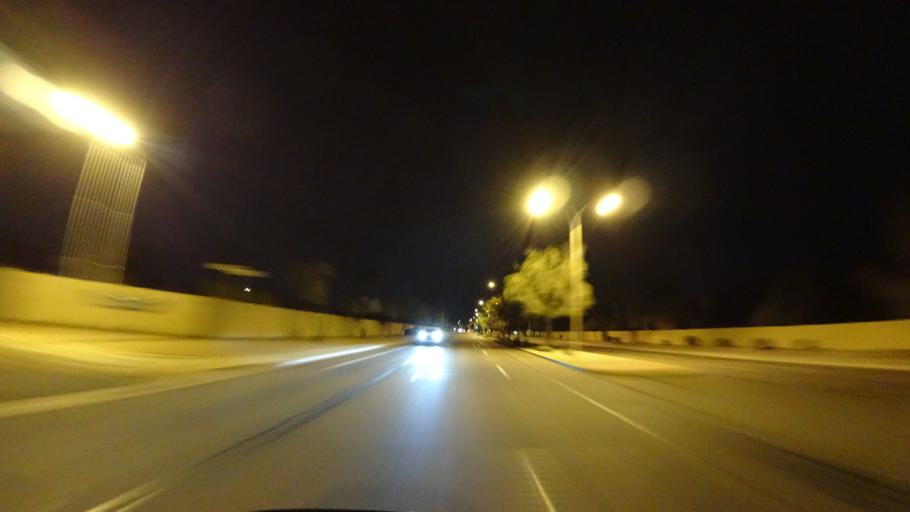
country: US
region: Arizona
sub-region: Maricopa County
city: Guadalupe
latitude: 33.3200
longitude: -111.9237
